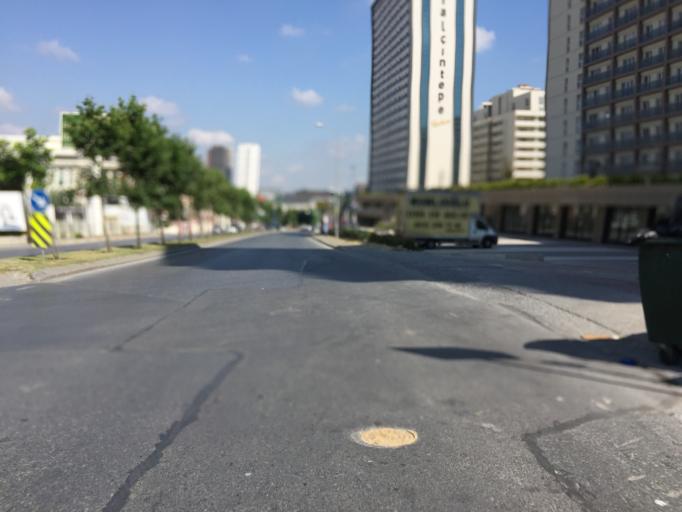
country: TR
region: Istanbul
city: Esenyurt
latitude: 41.0660
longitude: 28.6638
